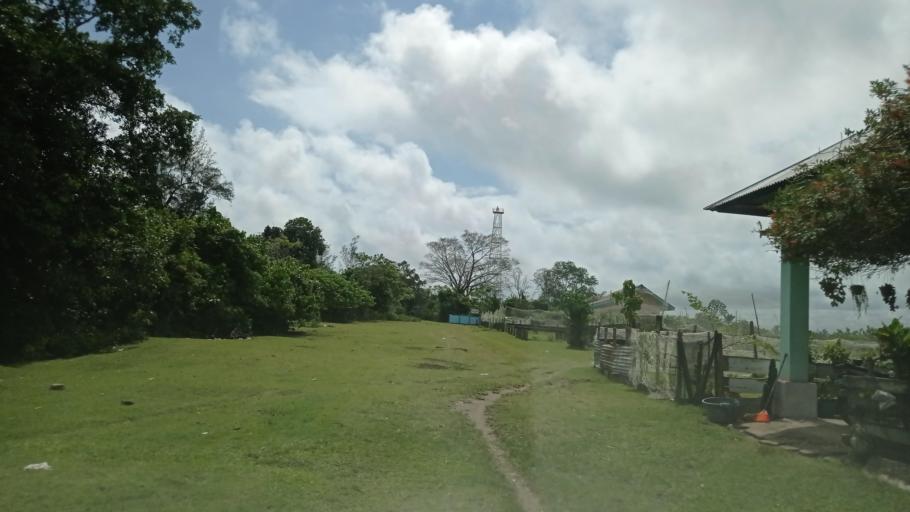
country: ID
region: Jambi
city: Sungai Penuh
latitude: -2.5466
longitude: 101.0850
